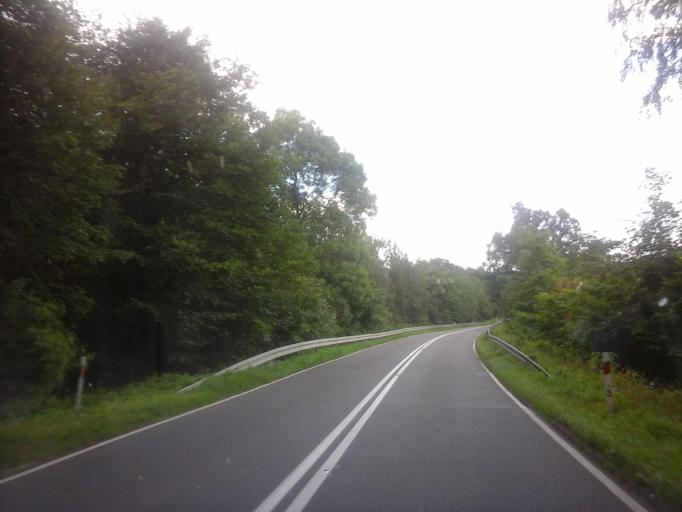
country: PL
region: West Pomeranian Voivodeship
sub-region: Powiat stargardzki
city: Suchan
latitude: 53.2588
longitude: 15.3331
